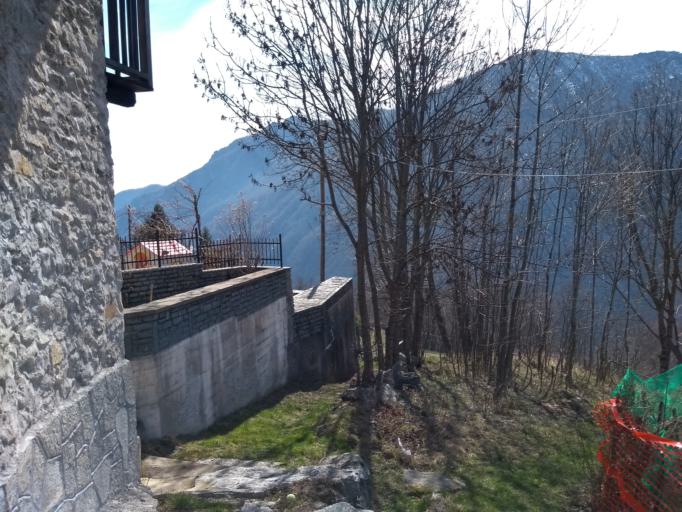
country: IT
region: Piedmont
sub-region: Provincia di Torino
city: Chialamberto
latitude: 45.3684
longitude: 7.3476
